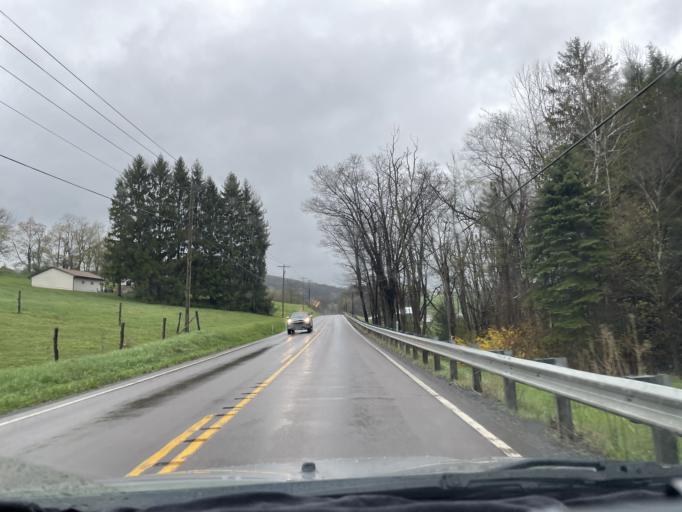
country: US
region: Maryland
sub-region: Garrett County
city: Mountain Lake Park
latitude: 39.4439
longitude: -79.2765
